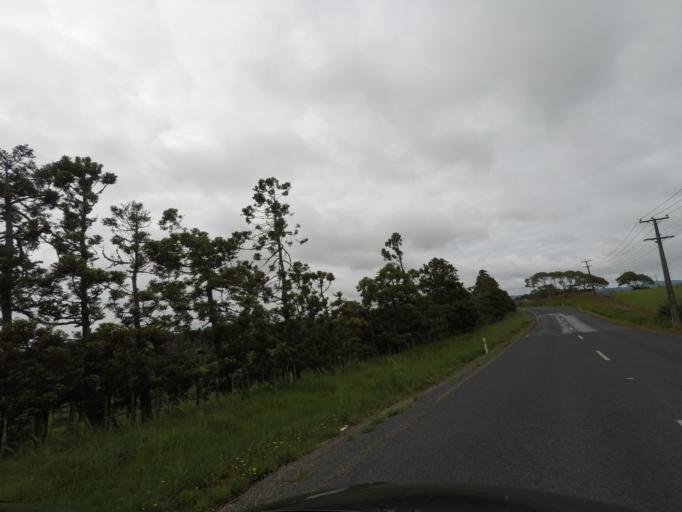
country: NZ
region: Auckland
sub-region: Auckland
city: Rosebank
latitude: -36.8247
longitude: 174.5770
